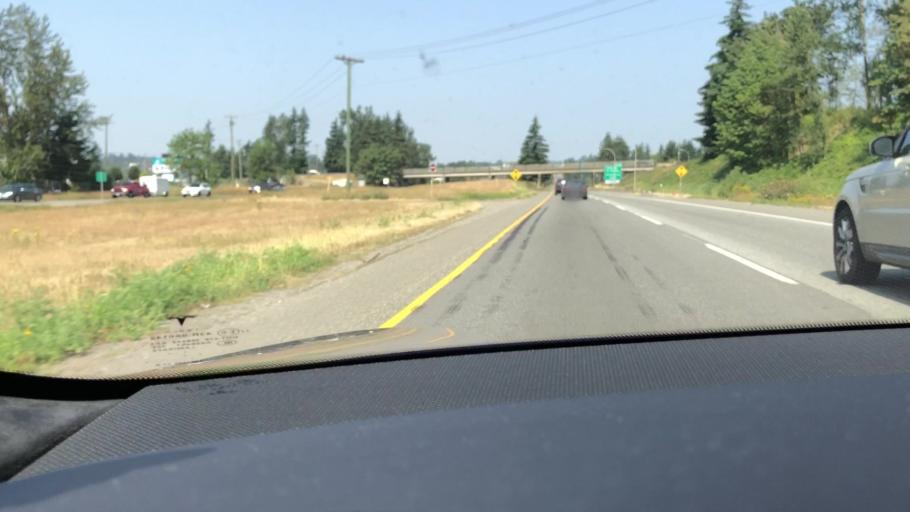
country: US
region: Washington
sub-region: Whatcom County
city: Sumas
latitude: 49.0455
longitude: -122.3523
